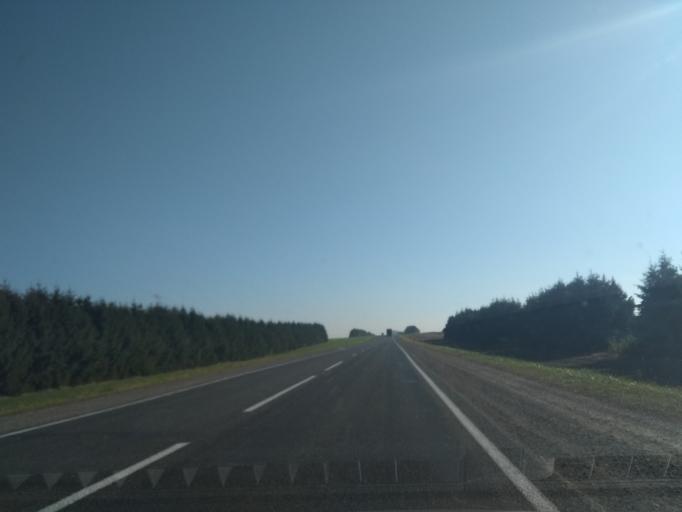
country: BY
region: Grodnenskaya
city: Zel'va
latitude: 53.1240
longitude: 25.0640
